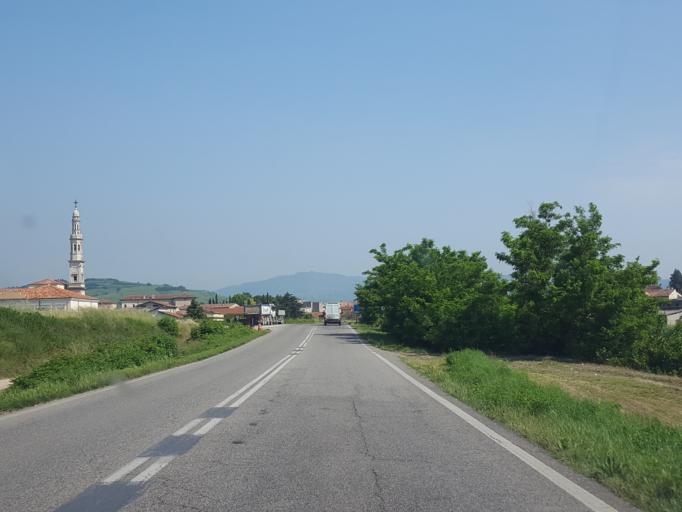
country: IT
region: Veneto
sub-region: Provincia di Verona
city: Monteforte d'Alpone
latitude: 45.4175
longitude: 11.2868
